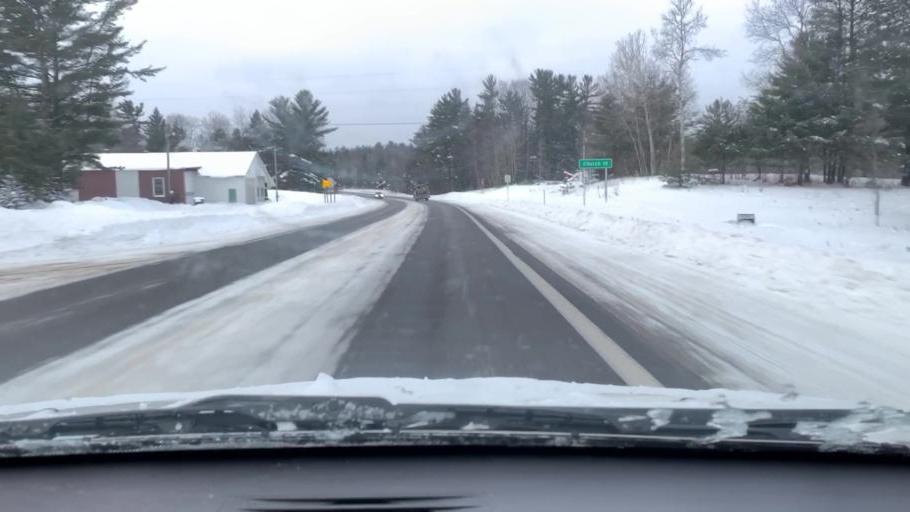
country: US
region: Michigan
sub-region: Kalkaska County
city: Kalkaska
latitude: 44.6452
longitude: -85.2804
